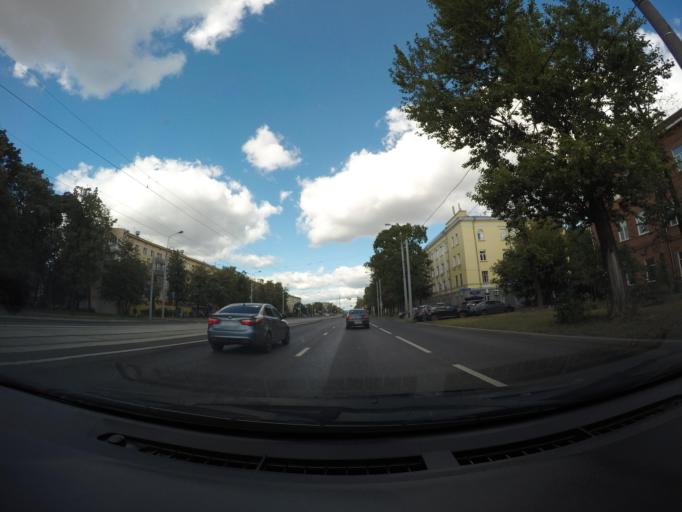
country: RU
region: Moscow
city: Lefortovo
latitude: 55.7661
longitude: 37.7319
